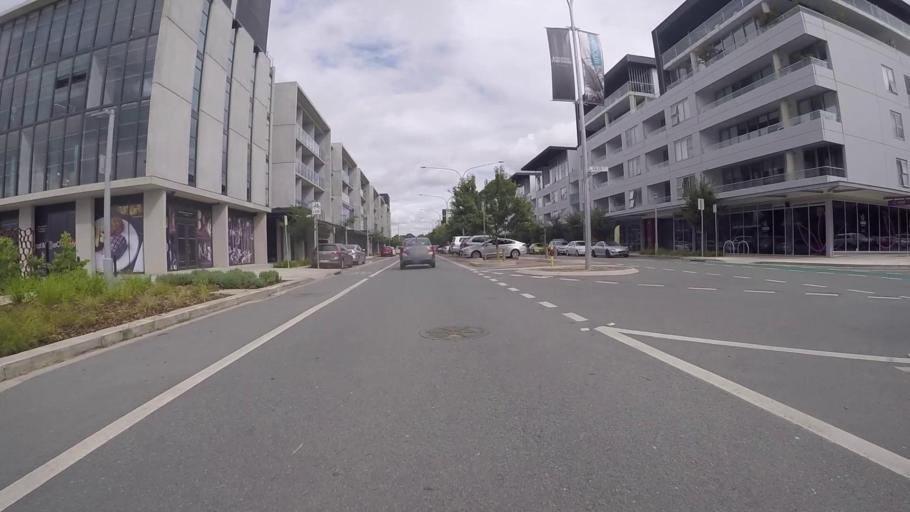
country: AU
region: Australian Capital Territory
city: Forrest
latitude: -35.3129
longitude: 149.1464
